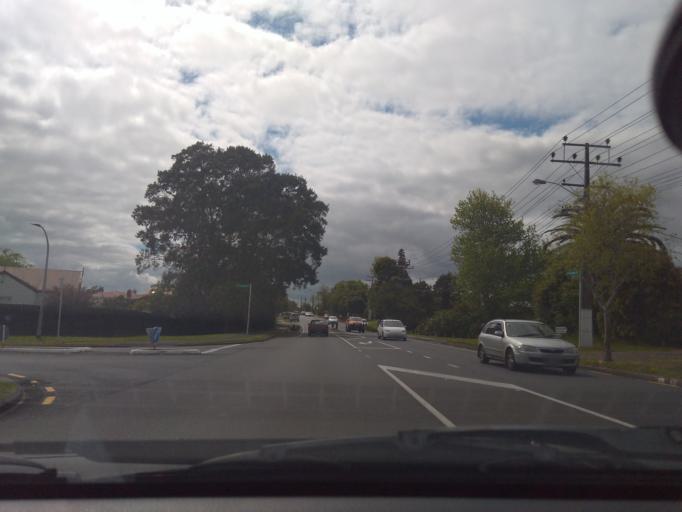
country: NZ
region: Auckland
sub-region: Auckland
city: Rosebank
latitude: -36.8643
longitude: 174.5979
